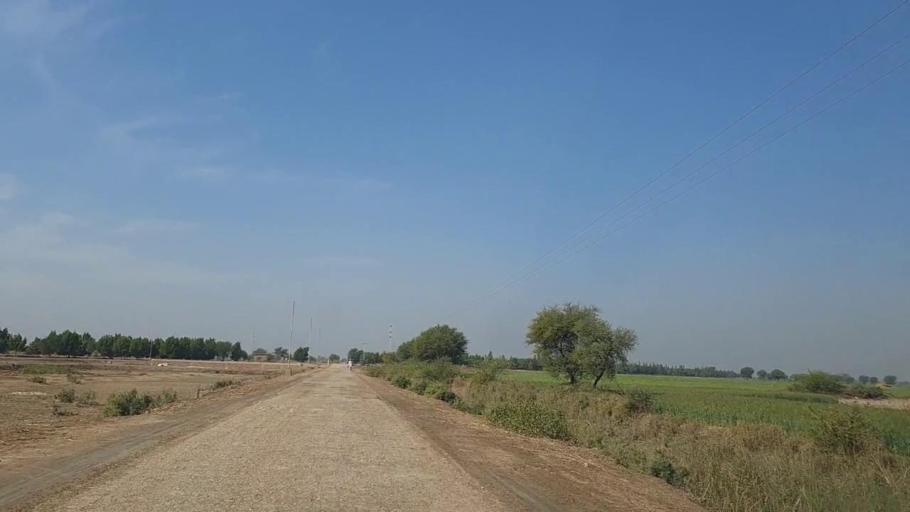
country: PK
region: Sindh
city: Mirpur Khas
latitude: 25.4825
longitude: 68.9848
